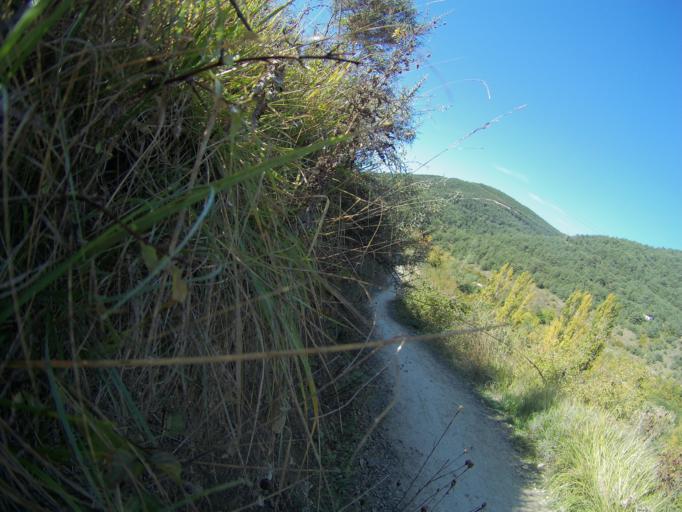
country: ES
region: Navarre
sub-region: Provincia de Navarra
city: Egues-Uharte
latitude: 42.8653
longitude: -1.5697
